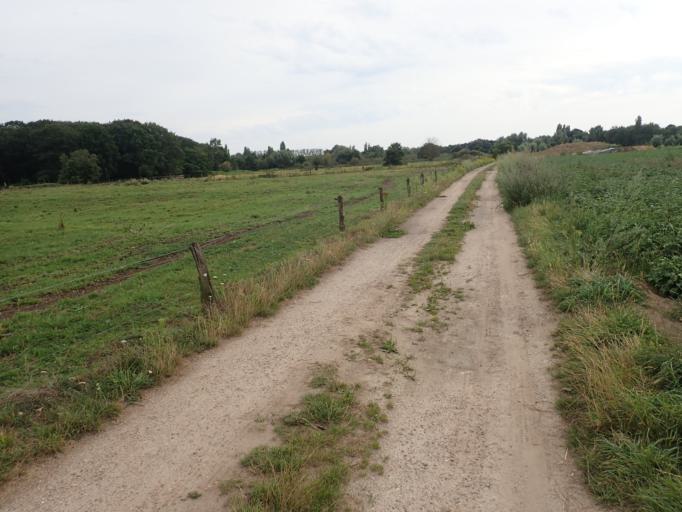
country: BE
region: Flanders
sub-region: Provincie Antwerpen
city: Ranst
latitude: 51.2136
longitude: 4.5598
